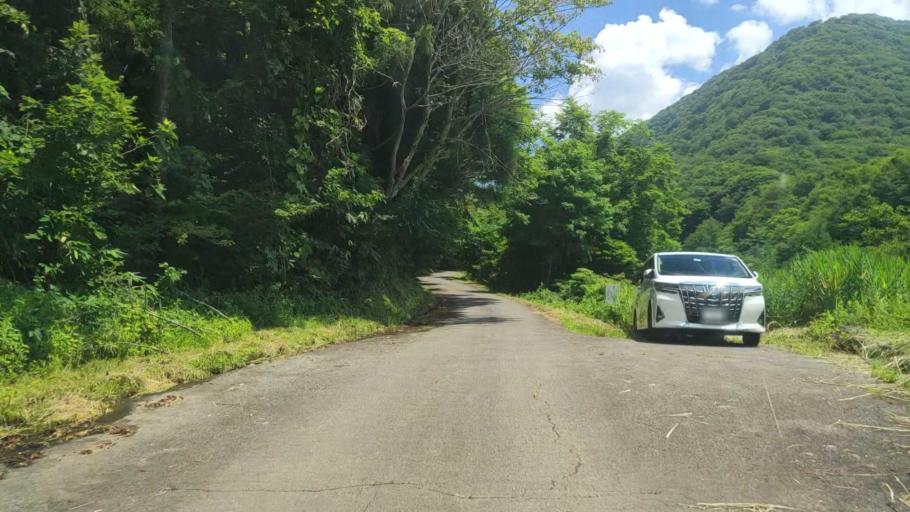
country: JP
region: Fukui
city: Ono
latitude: 35.7923
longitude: 136.5007
